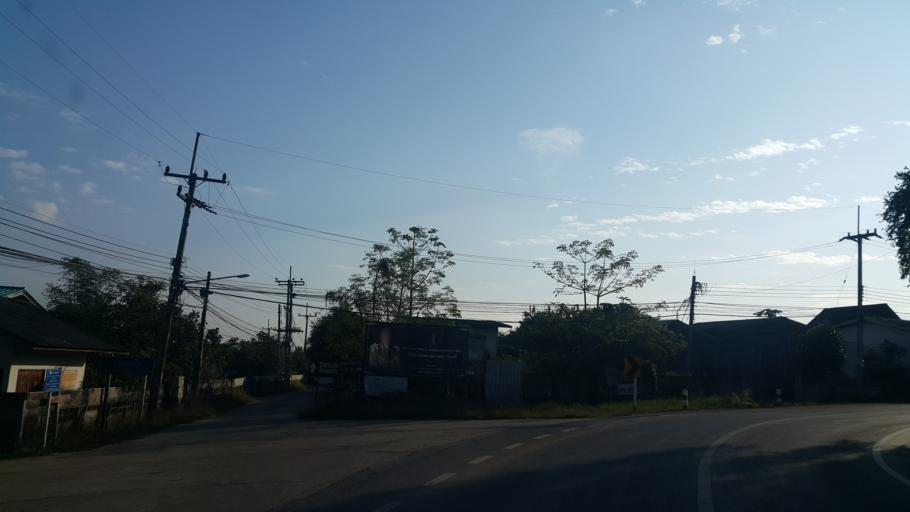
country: TH
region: Lampang
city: Soem Ngam
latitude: 18.0954
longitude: 99.3412
